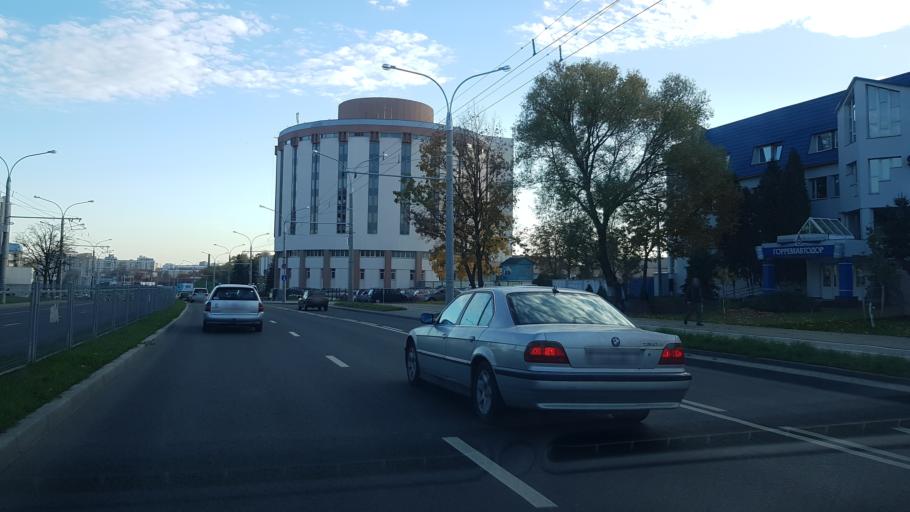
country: BY
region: Minsk
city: Minsk
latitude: 53.9014
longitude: 27.5341
